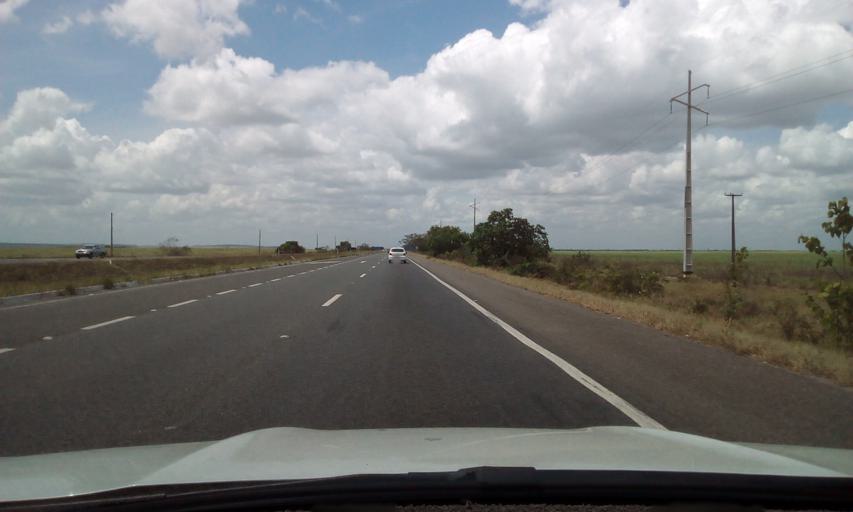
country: BR
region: Paraiba
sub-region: Cruz Do Espirito Santo
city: Cruz do Espirito Santo
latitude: -7.1808
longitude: -35.0492
